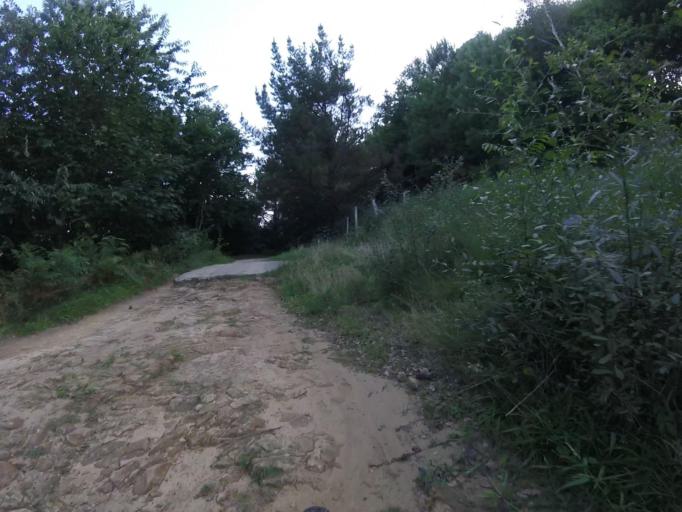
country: ES
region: Basque Country
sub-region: Provincia de Guipuzcoa
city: Fuenterrabia
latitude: 43.3652
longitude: -1.8244
